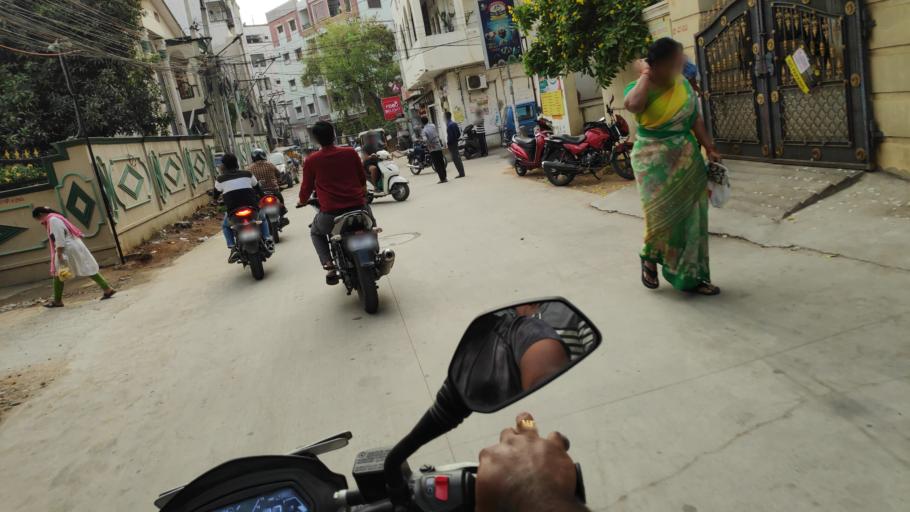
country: IN
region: Telangana
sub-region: Rangareddi
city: Kukatpalli
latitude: 17.4839
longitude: 78.4113
